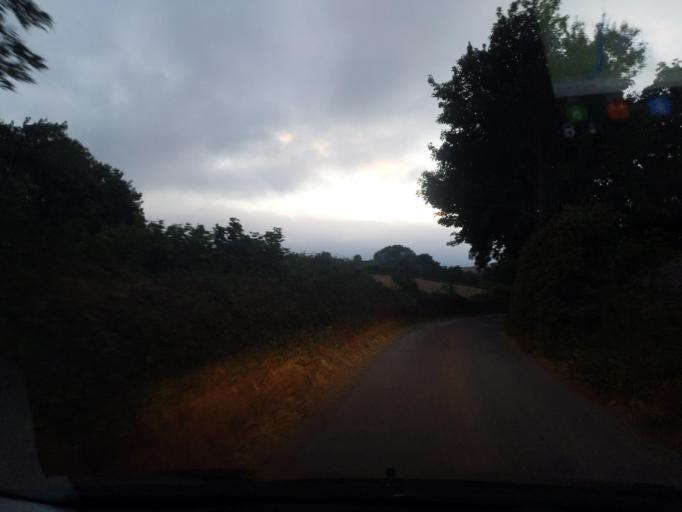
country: GB
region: England
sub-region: Devon
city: Ipplepen
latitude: 50.4798
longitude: -3.6164
